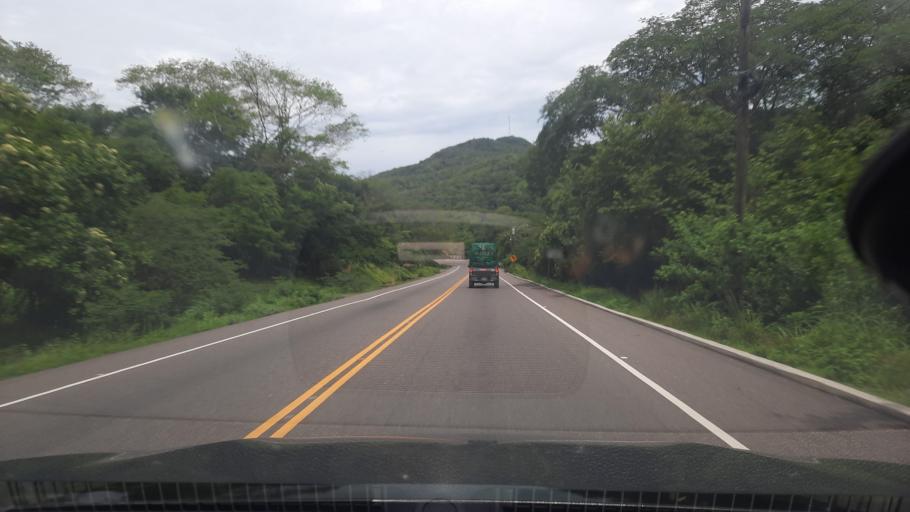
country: HN
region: Valle
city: Goascoran
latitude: 13.5654
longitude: -87.6713
